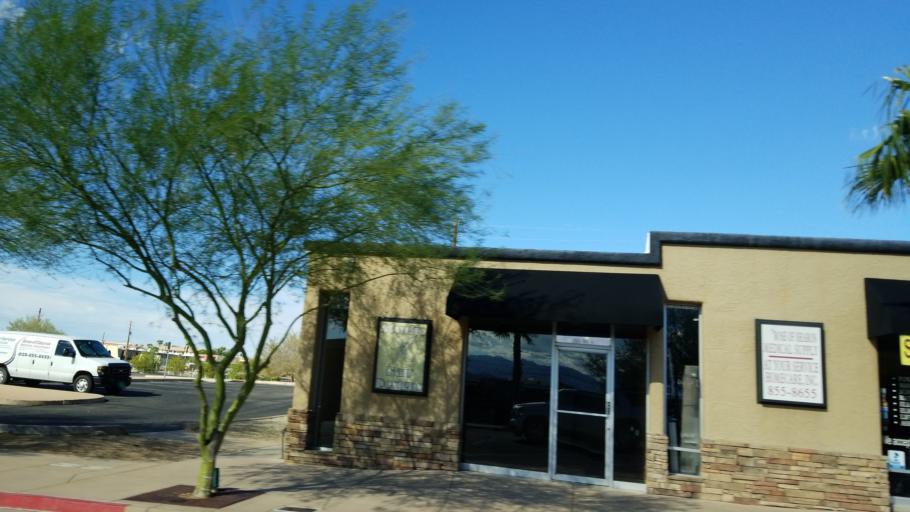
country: US
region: Arizona
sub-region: Mohave County
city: Lake Havasu City
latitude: 34.4749
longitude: -114.3263
